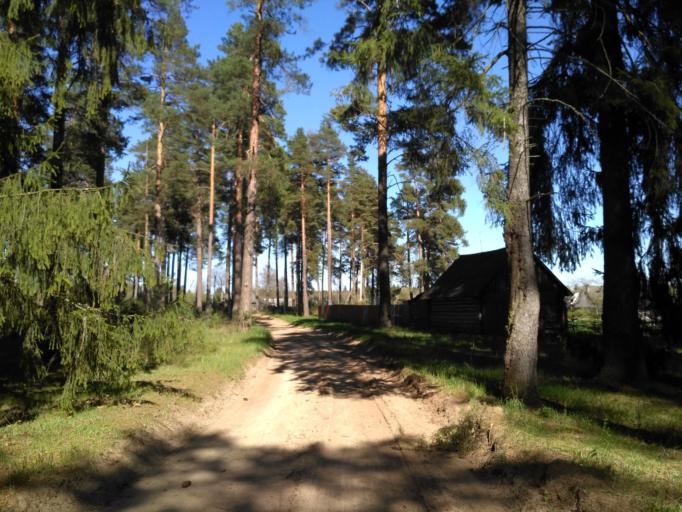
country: BY
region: Minsk
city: Horad Barysaw
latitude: 54.5227
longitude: 28.5337
